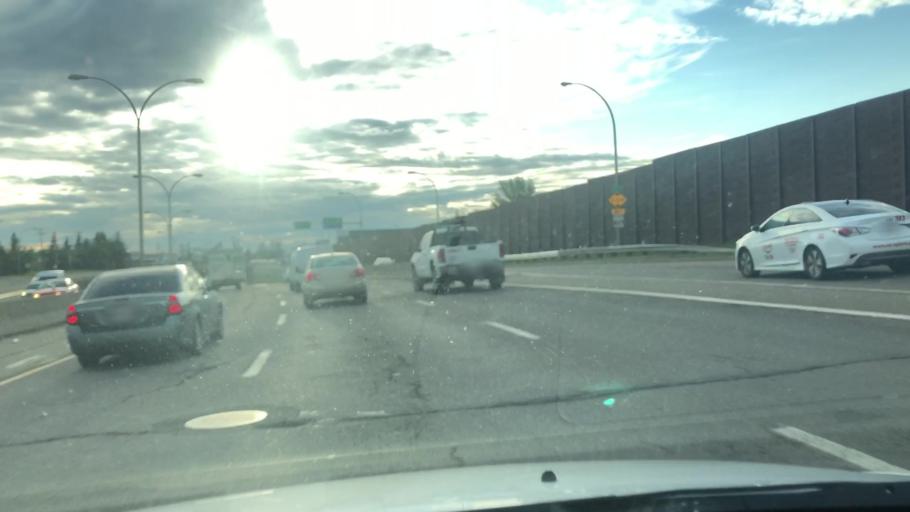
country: CA
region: Alberta
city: Edmonton
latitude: 53.5813
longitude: -113.4718
